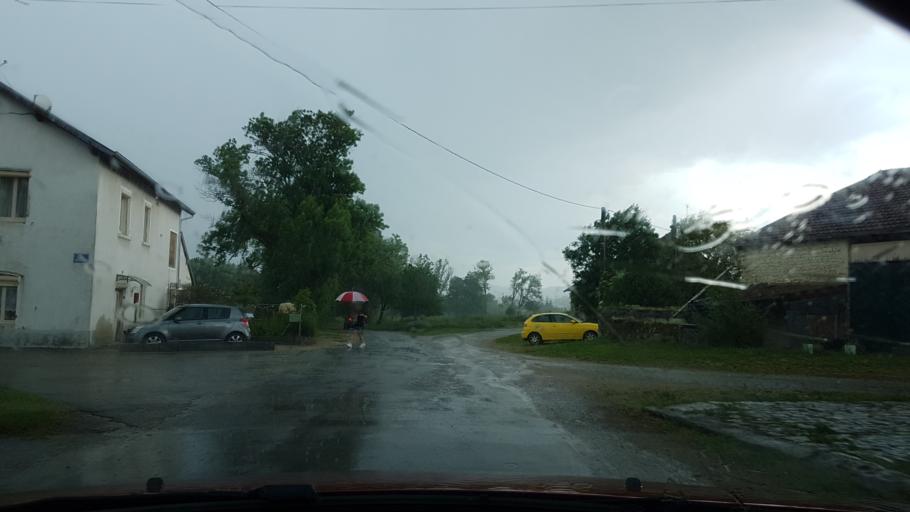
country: FR
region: Franche-Comte
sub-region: Departement du Jura
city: Clairvaux-les-Lacs
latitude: 46.5755
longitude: 5.6939
